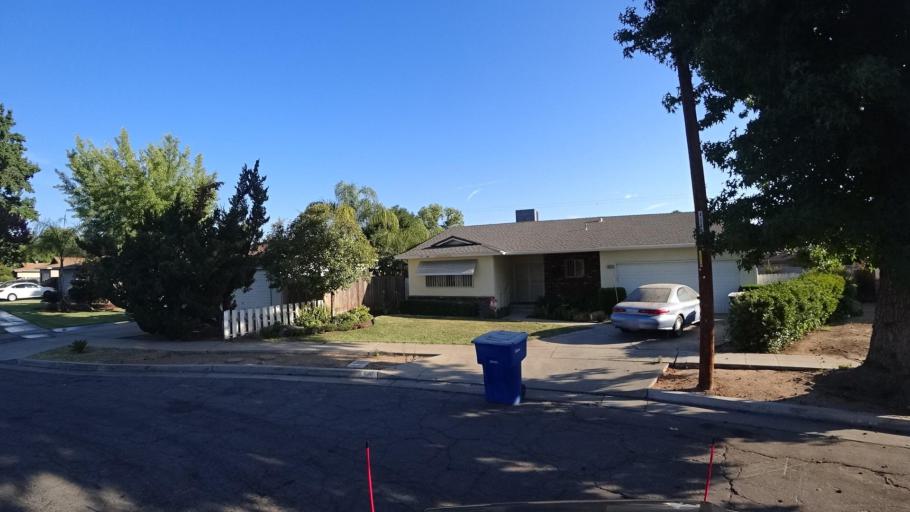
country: US
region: California
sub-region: Fresno County
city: Sunnyside
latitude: 36.7410
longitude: -119.7316
